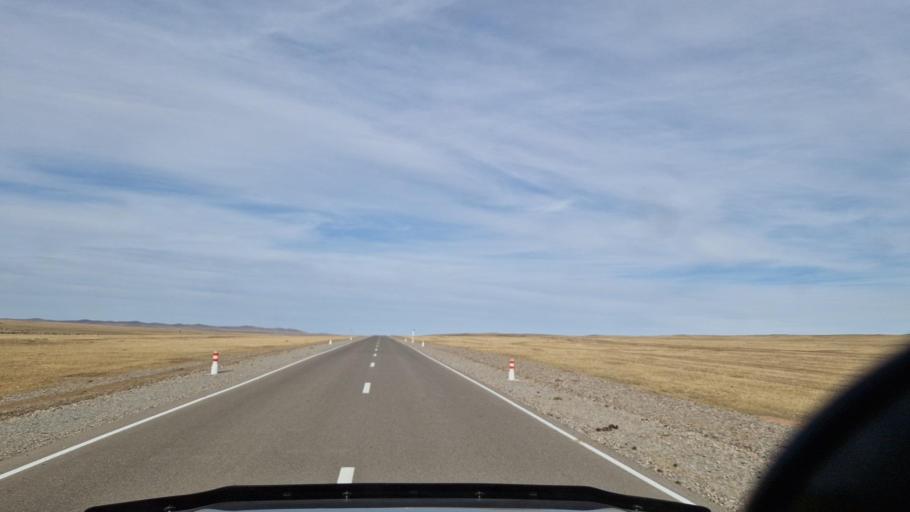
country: MN
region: Hentiy
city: Undurkhaan
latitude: 47.6546
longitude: 111.0204
